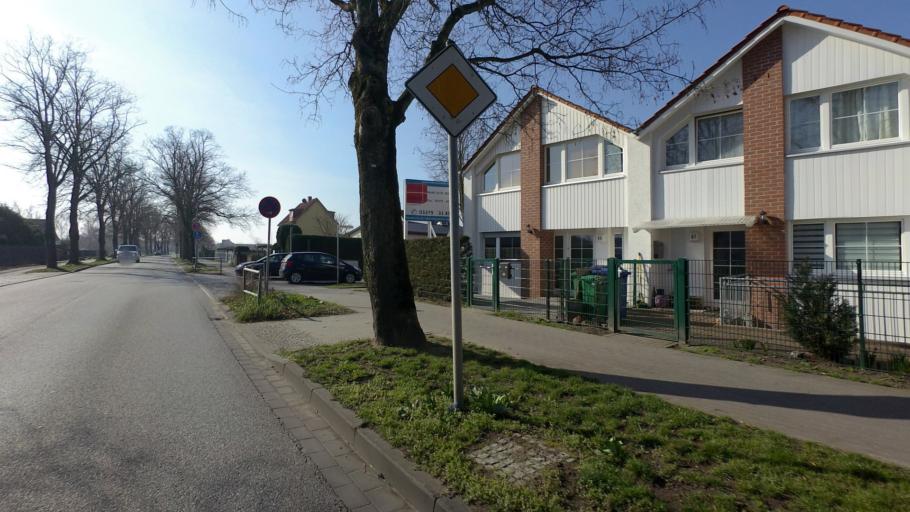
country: DE
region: Berlin
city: Gropiusstadt
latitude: 52.4061
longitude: 13.4408
